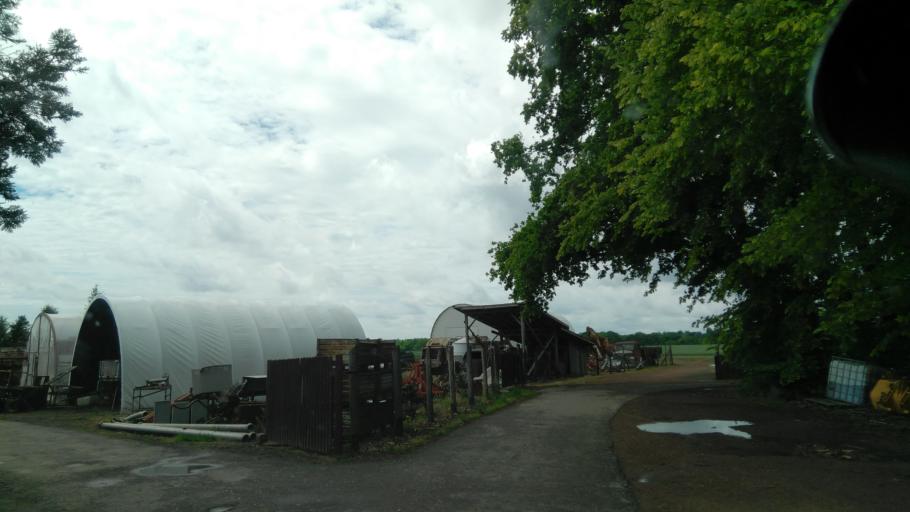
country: HU
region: Bekes
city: Bekescsaba
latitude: 46.6772
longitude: 21.1785
